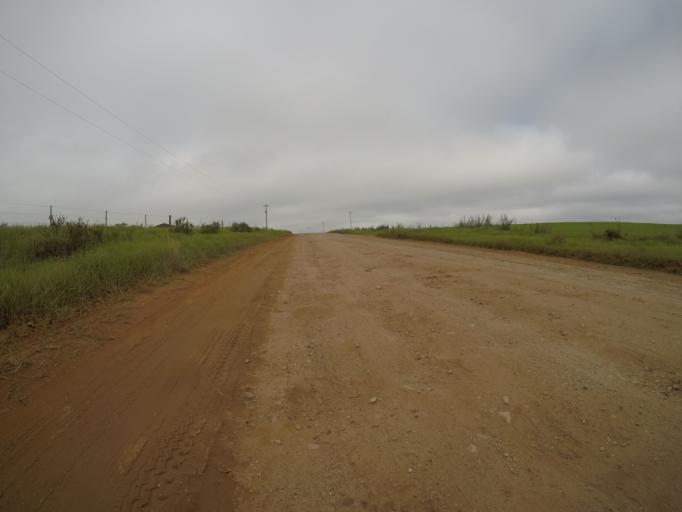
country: ZA
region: Eastern Cape
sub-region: Cacadu District Municipality
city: Kareedouw
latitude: -34.0227
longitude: 24.2405
